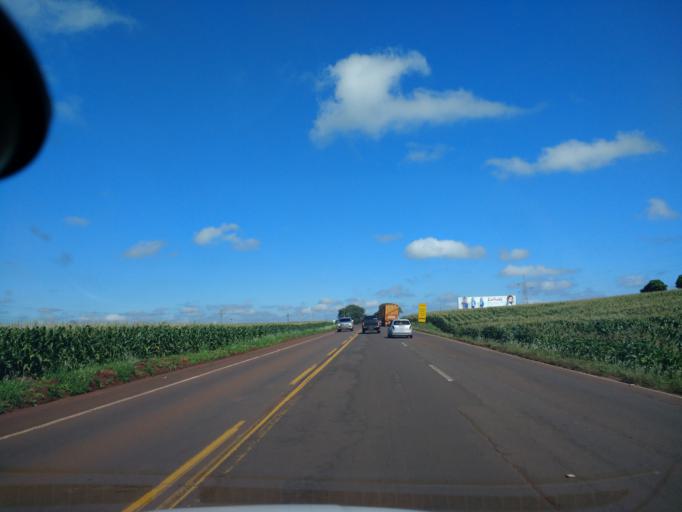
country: BR
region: Parana
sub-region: Cianorte
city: Cianorte
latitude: -23.6407
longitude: -52.4771
